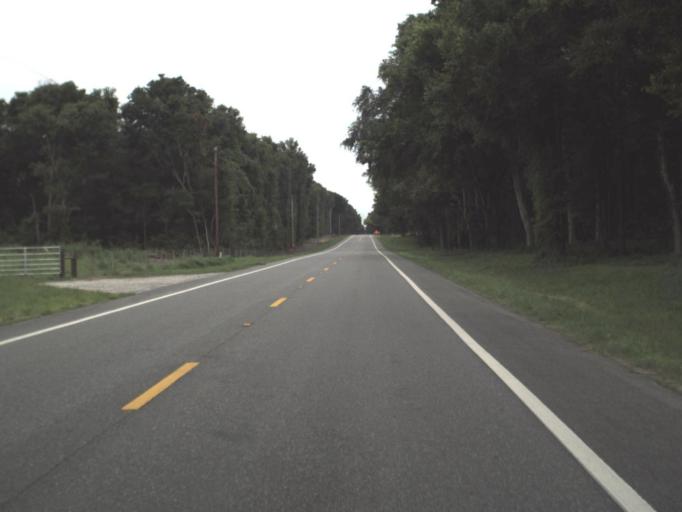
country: US
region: Florida
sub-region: Alachua County
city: Archer
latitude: 29.5586
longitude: -82.5336
